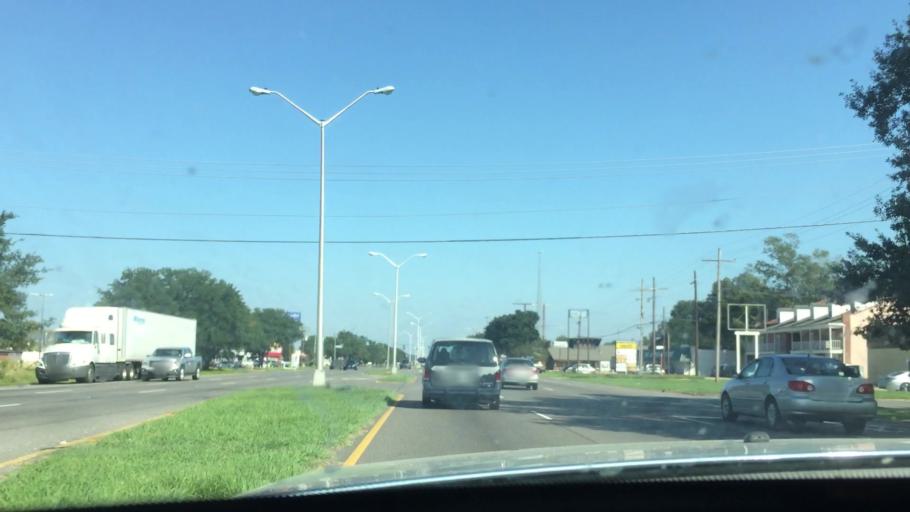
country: US
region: Louisiana
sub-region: East Baton Rouge Parish
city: Baton Rouge
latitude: 30.4514
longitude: -91.1213
